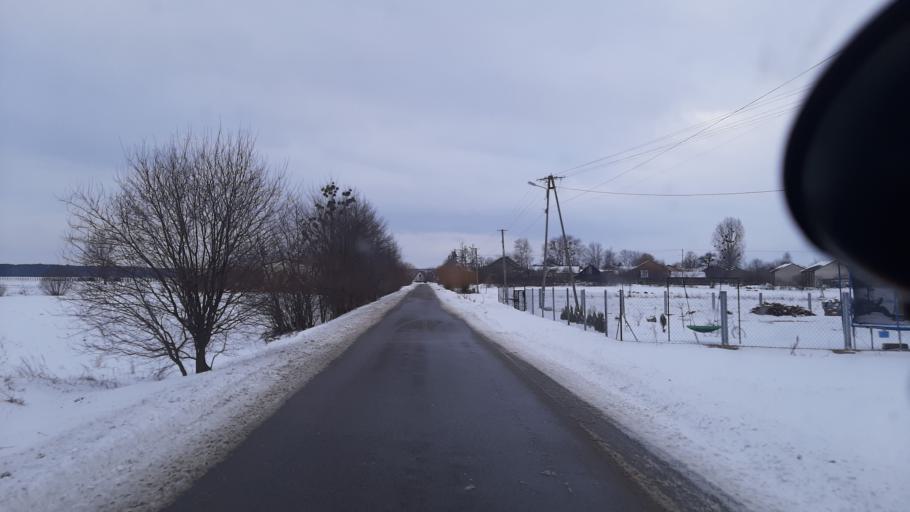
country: PL
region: Lublin Voivodeship
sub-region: Powiat lubartowski
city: Abramow
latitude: 51.4431
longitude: 22.2777
